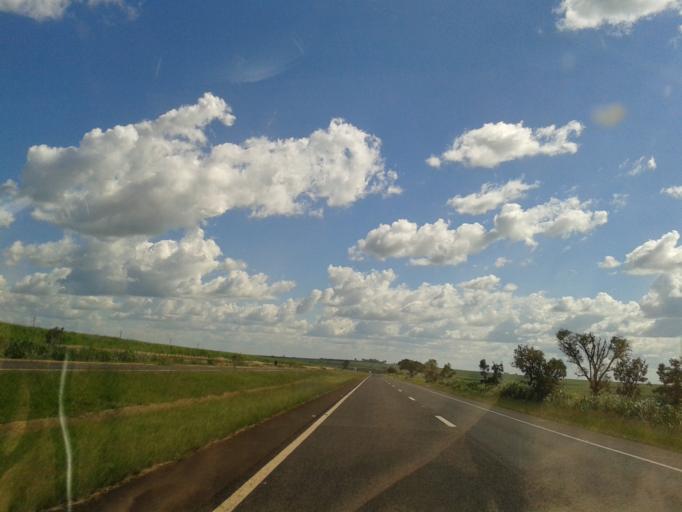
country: BR
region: Goias
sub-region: Morrinhos
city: Morrinhos
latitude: -17.8616
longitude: -49.2237
